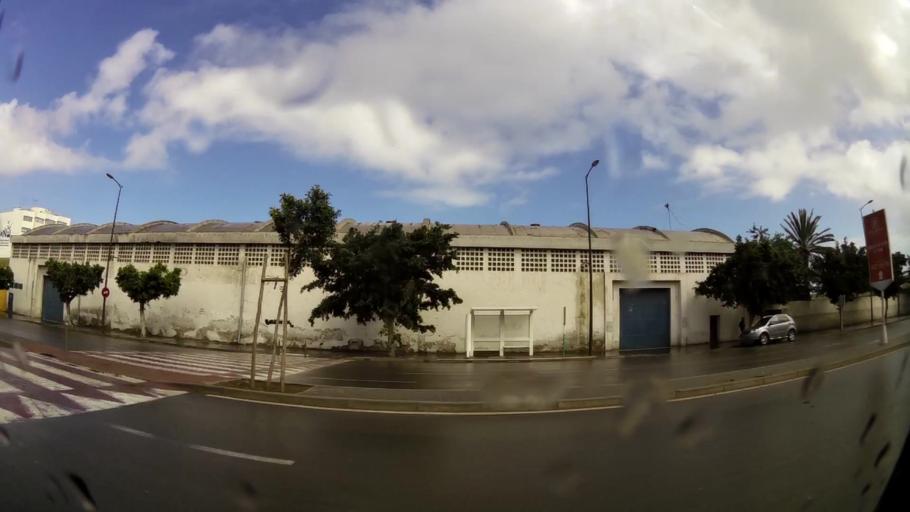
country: MA
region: Grand Casablanca
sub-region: Casablanca
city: Casablanca
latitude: 33.5969
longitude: -7.5961
